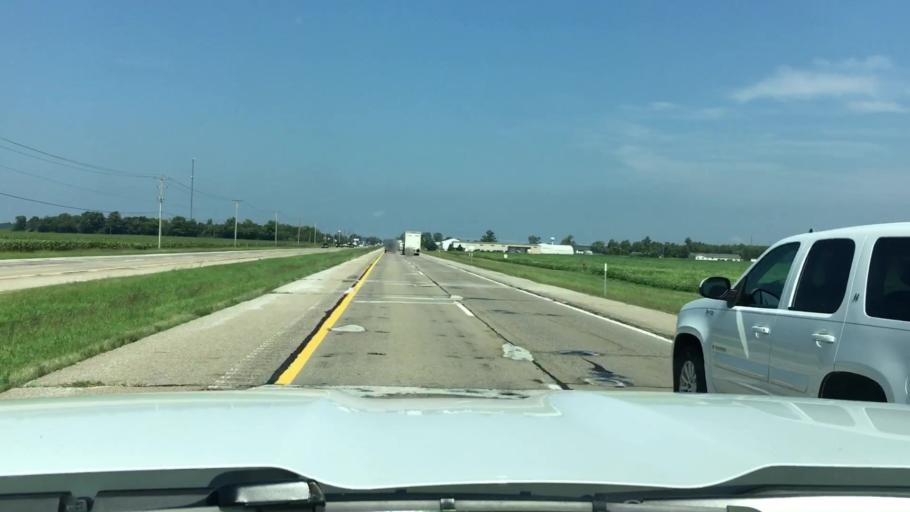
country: US
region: Michigan
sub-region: Kalamazoo County
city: Schoolcraft
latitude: 42.0841
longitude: -85.6366
